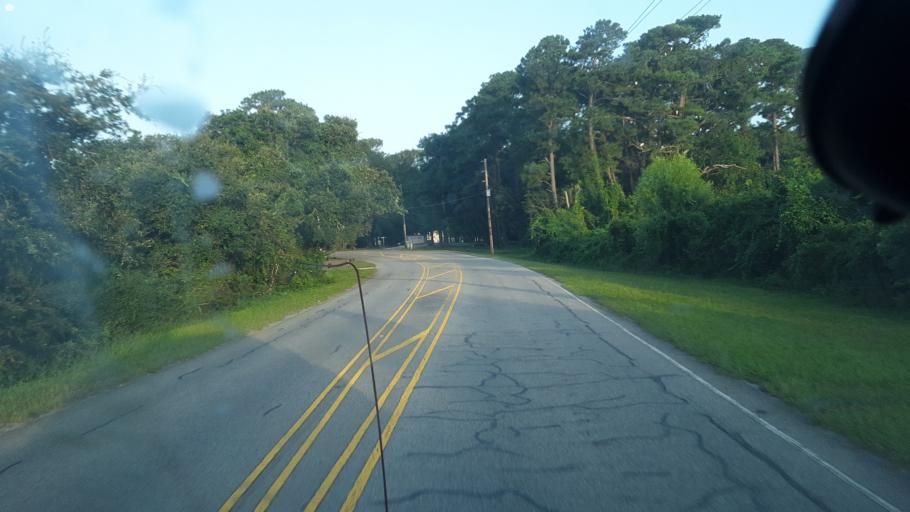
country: US
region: North Carolina
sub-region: Brunswick County
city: Sunset Beach
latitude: 33.8801
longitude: -78.5315
